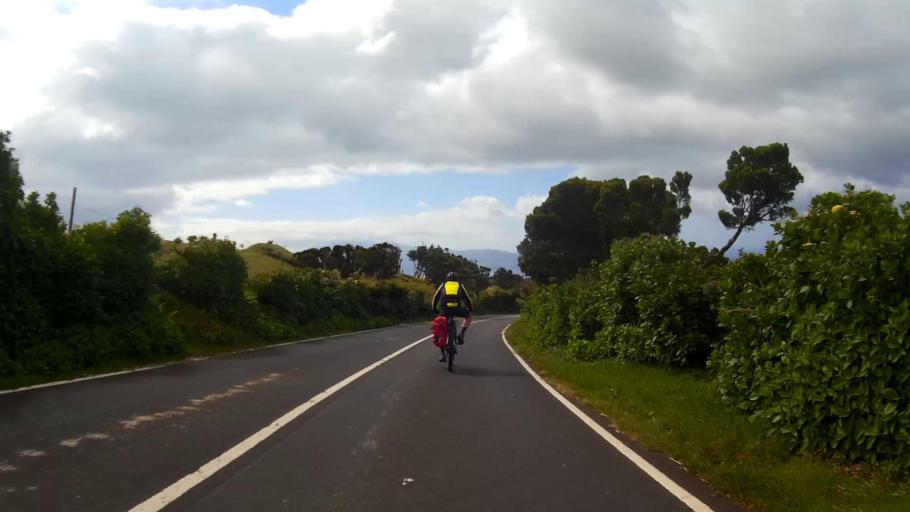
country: PT
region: Azores
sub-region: Madalena
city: Madalena
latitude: 38.4967
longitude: -28.4602
